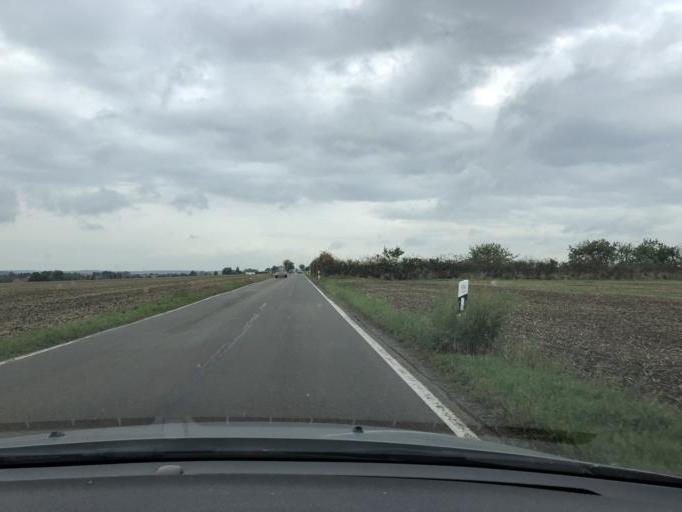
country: DE
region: Saxony-Anhalt
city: Goseck
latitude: 51.2141
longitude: 11.8837
